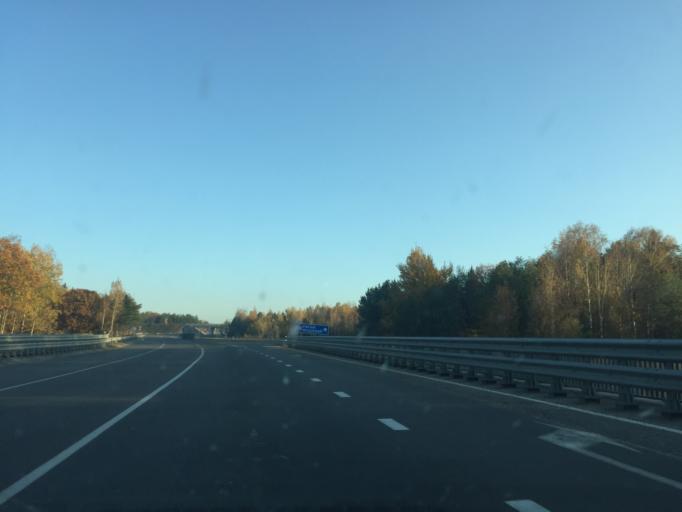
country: BY
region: Mogilev
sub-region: Mahilyowski Rayon
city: Kadino
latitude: 53.9019
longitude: 30.4731
